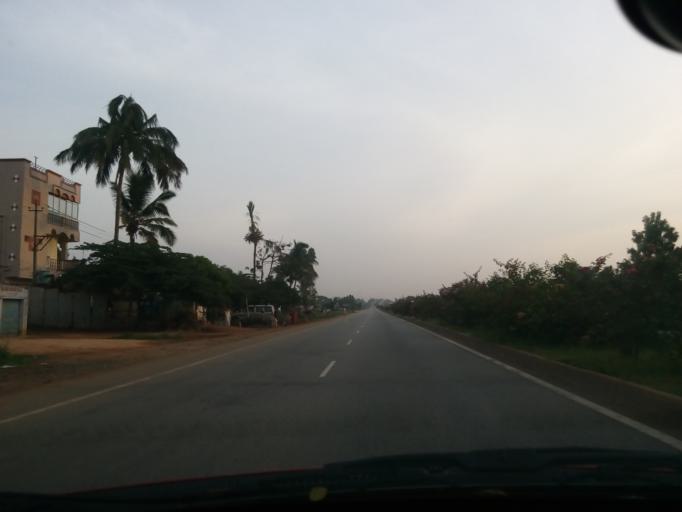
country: IN
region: Karnataka
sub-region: Bangalore Rural
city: Vijayapura
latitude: 13.3391
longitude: 77.7255
